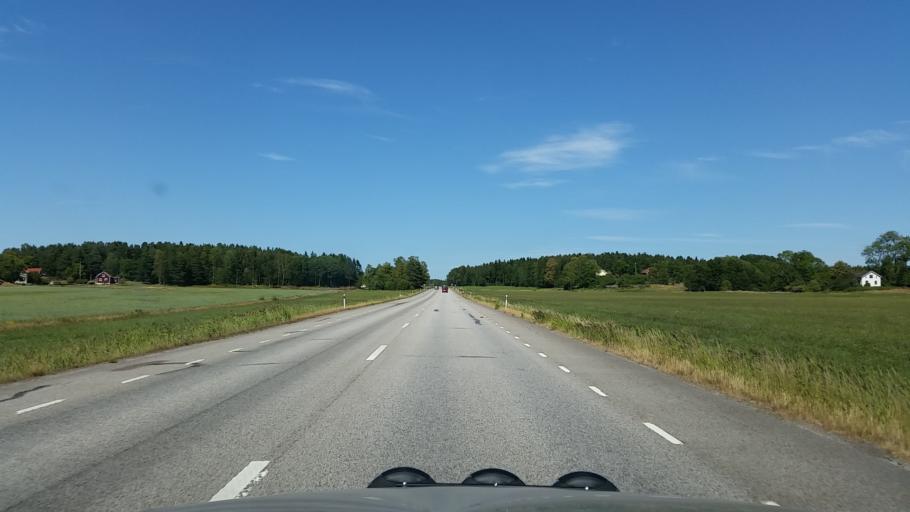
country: SE
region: Vaestra Goetaland
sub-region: Amals Kommun
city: Amal
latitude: 59.0027
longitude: 12.6843
